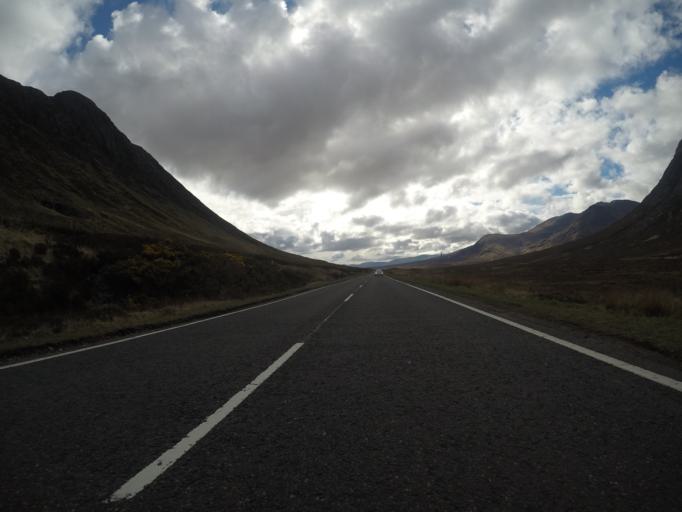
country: GB
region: Scotland
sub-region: Highland
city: Spean Bridge
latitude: 56.6631
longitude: -4.8972
